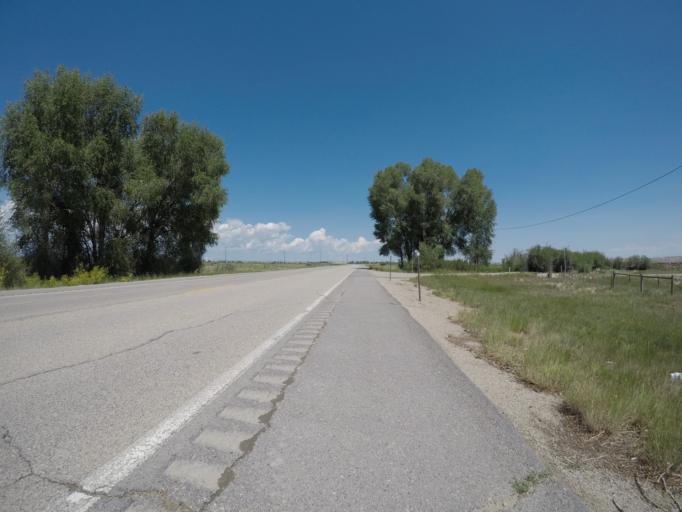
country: US
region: Wyoming
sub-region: Sublette County
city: Marbleton
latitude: 42.5249
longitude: -110.1085
